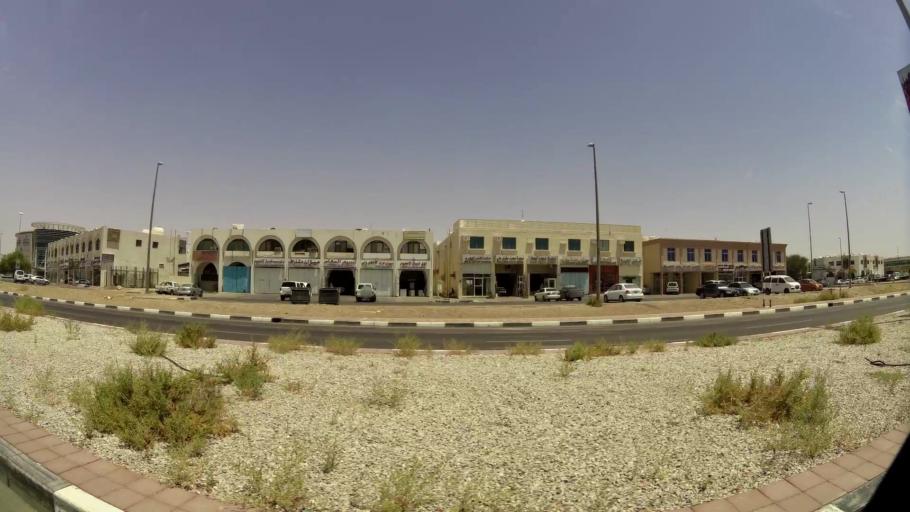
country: OM
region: Al Buraimi
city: Al Buraymi
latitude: 24.2630
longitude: 55.7686
